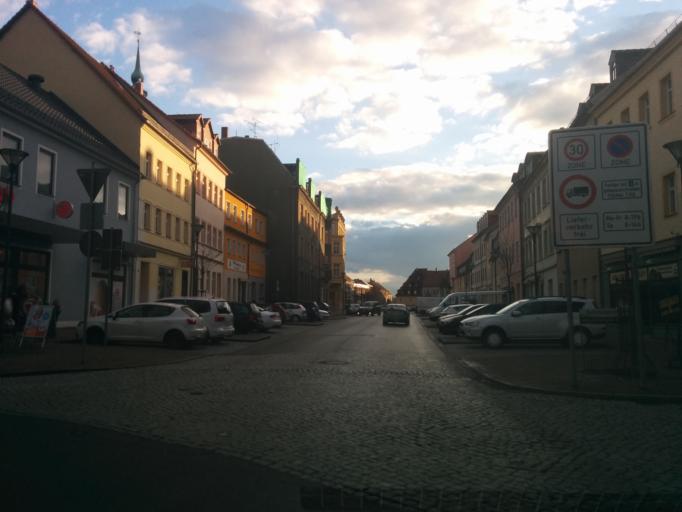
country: DE
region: Saxony
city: Frankenberg
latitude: 50.9140
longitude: 13.0334
